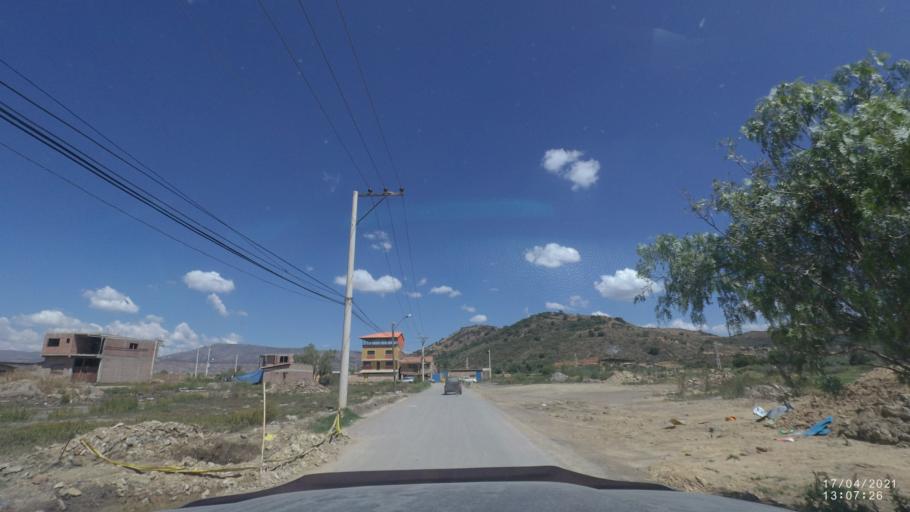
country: BO
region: Cochabamba
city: Cochabamba
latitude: -17.4132
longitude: -66.2239
